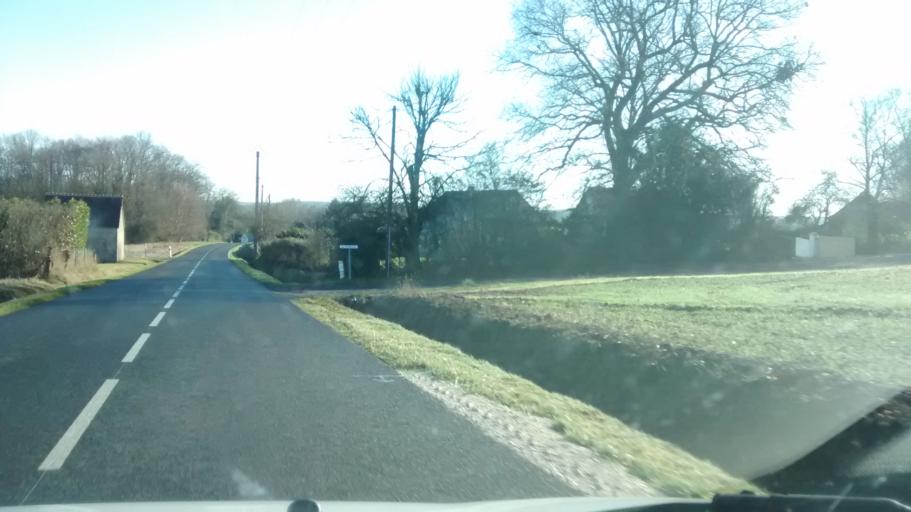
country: FR
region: Centre
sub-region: Departement d'Indre-et-Loire
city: Reugny
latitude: 47.4848
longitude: 0.8491
